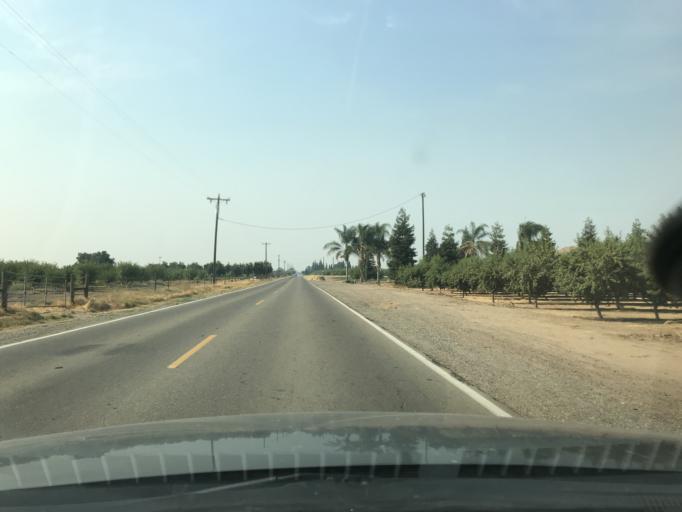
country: US
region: California
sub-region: Merced County
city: Atwater
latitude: 37.3063
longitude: -120.6147
